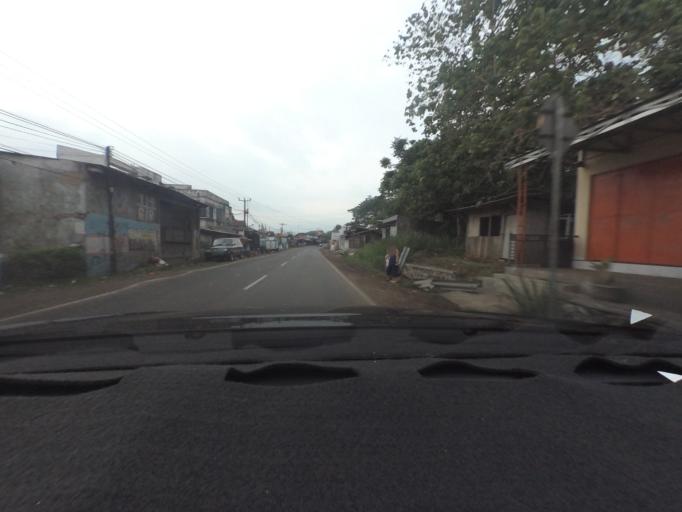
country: ID
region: West Java
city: Cicurug
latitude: -6.8081
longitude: 106.7699
